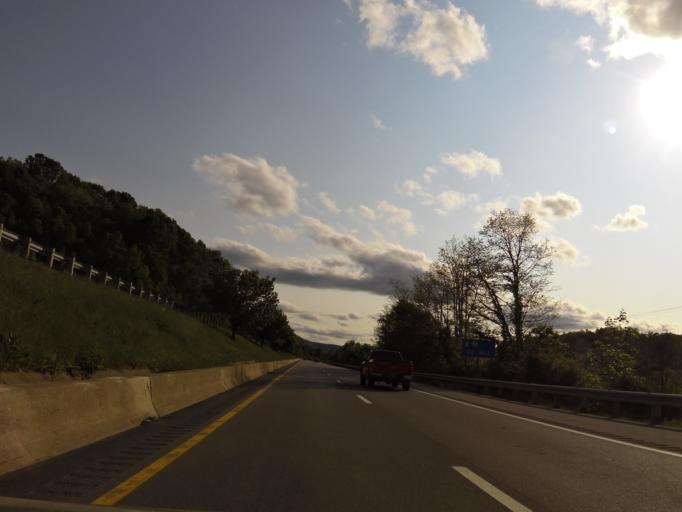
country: US
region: West Virginia
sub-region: Mercer County
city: Bluefield
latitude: 37.2663
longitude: -81.1805
